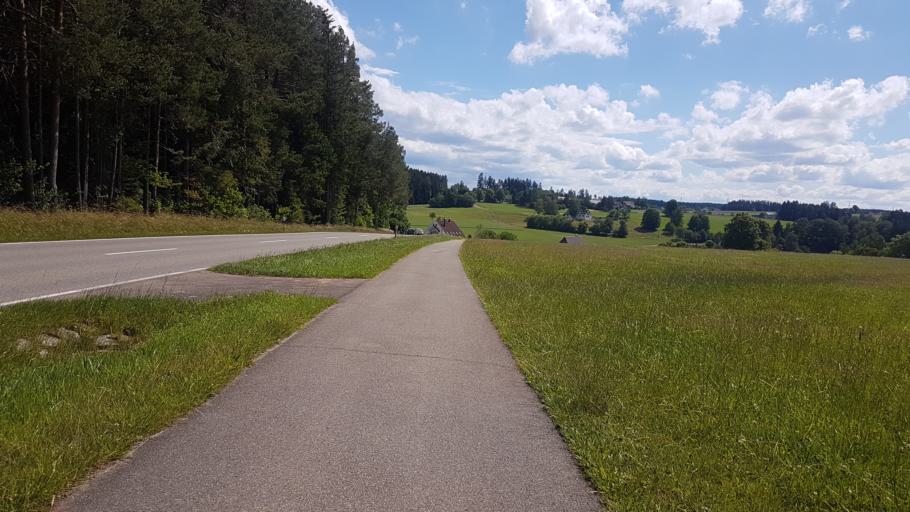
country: DE
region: Baden-Wuerttemberg
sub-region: Freiburg Region
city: Hardt
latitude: 48.1979
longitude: 8.4132
